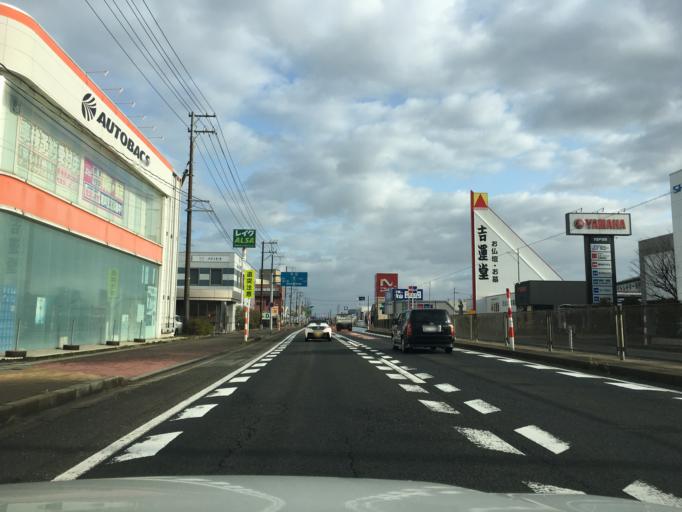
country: JP
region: Yamagata
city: Sakata
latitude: 38.8995
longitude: 139.8557
